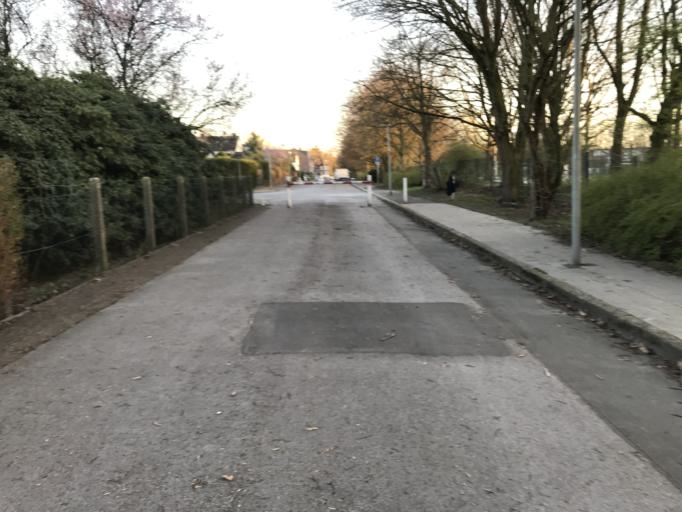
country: DE
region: North Rhine-Westphalia
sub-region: Regierungsbezirk Munster
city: Bottrop
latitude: 51.4944
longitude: 6.9179
